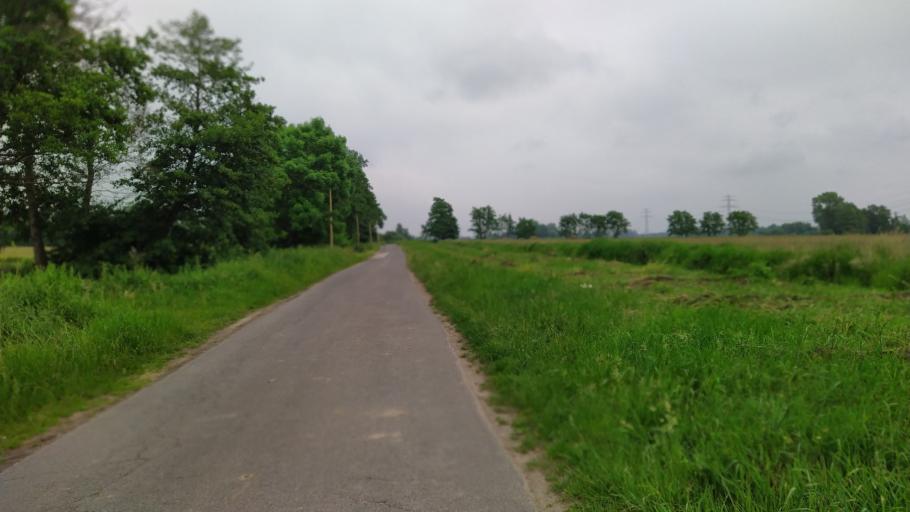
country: DE
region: Lower Saxony
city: Neu Wulmstorf
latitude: 53.4935
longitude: 9.7864
